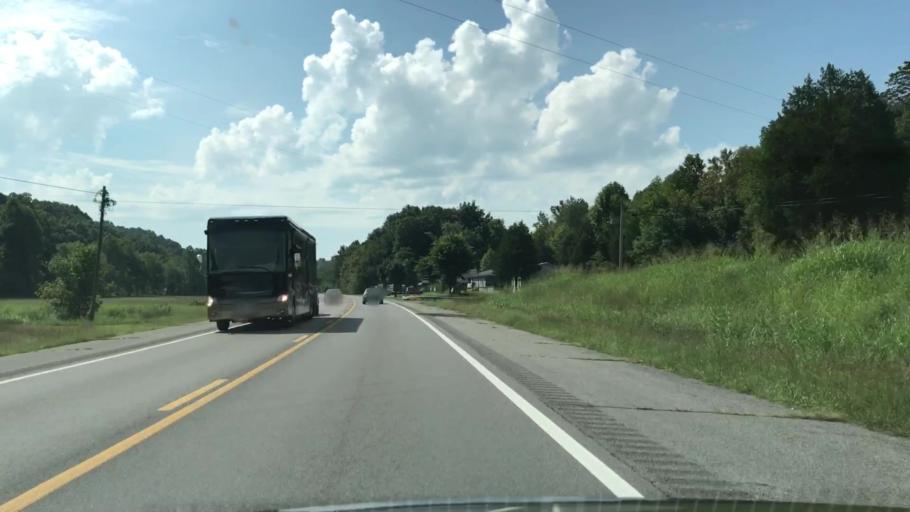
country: US
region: Tennessee
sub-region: Sumner County
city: Westmoreland
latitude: 36.6362
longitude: -86.2428
